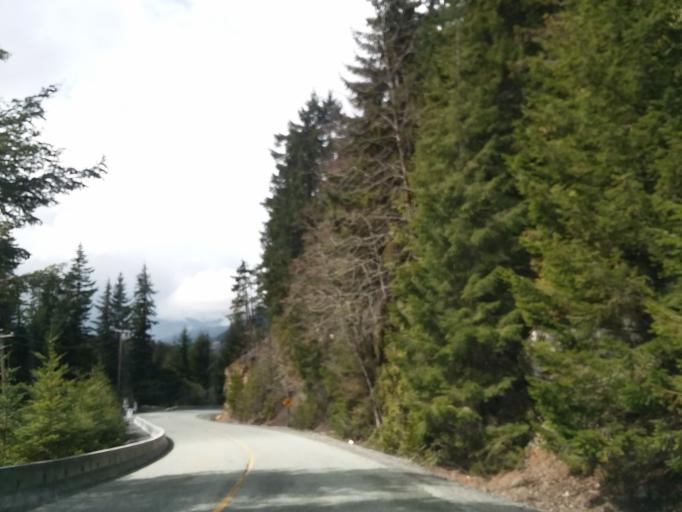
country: CA
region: British Columbia
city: Whistler
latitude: 50.0947
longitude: -123.0060
